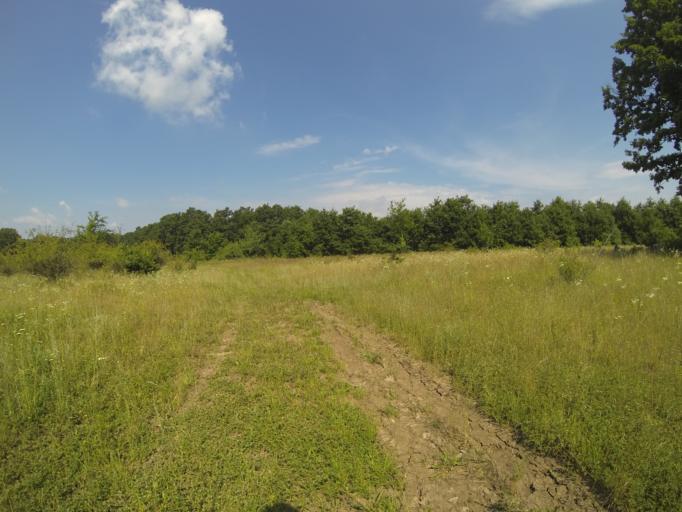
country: RO
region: Gorj
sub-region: Comuna Crusetu
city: Crusetu
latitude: 44.6147
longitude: 23.6306
